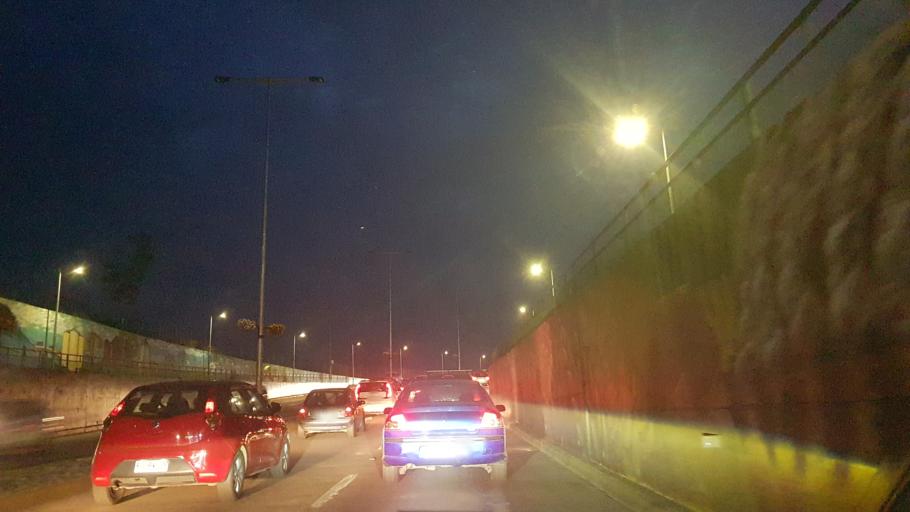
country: CL
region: Santiago Metropolitan
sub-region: Provincia de Santiago
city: Lo Prado
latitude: -33.3564
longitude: -70.7113
